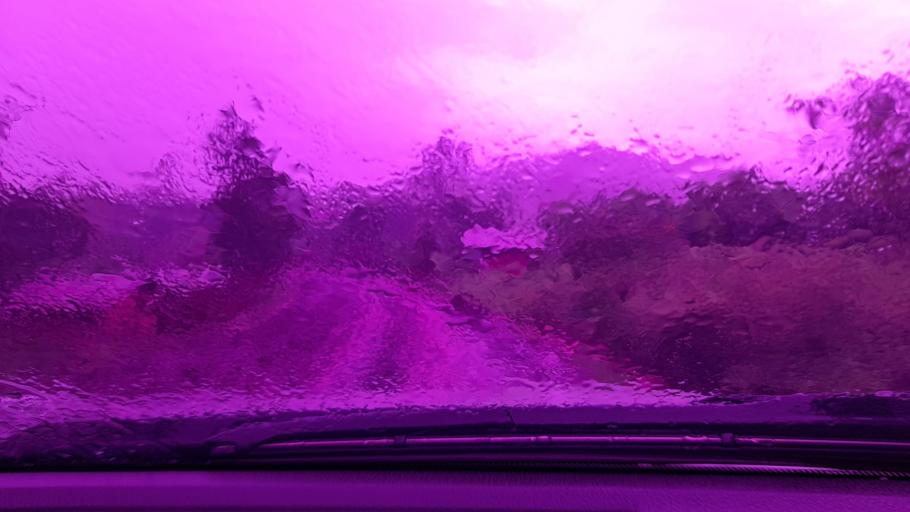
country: ET
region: Oromiya
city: Metu
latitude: 8.3519
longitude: 35.5991
